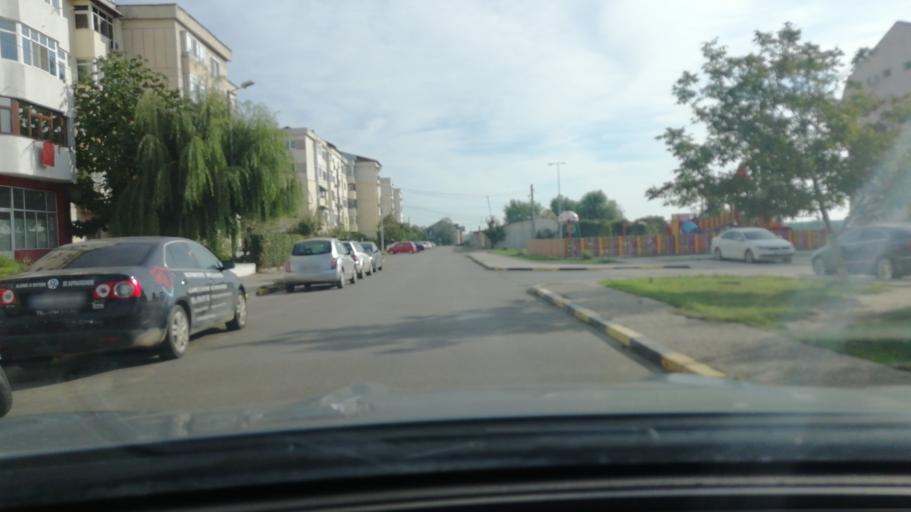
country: RO
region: Galati
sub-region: Municipiul Tecuci
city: Tecuci
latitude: 45.8269
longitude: 27.4380
